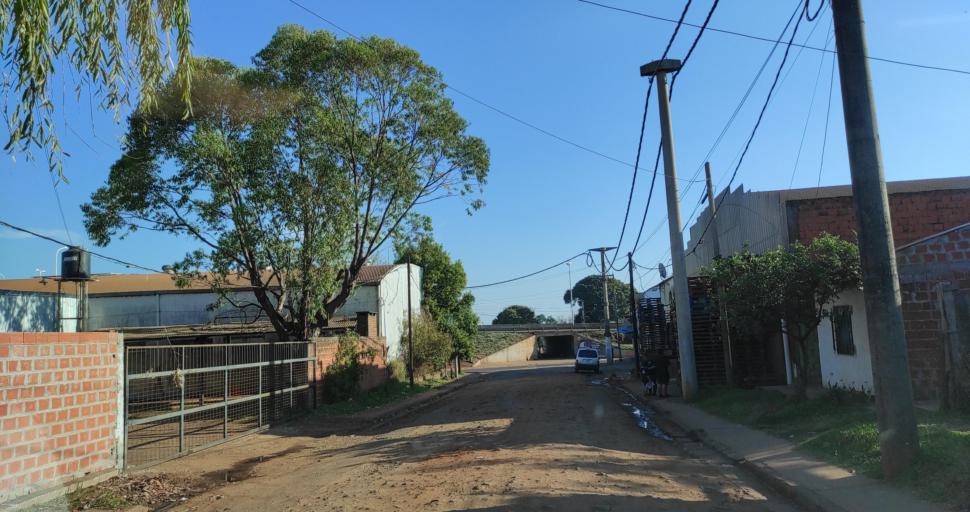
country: AR
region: Misiones
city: Garupa
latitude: -27.4516
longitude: -55.8646
